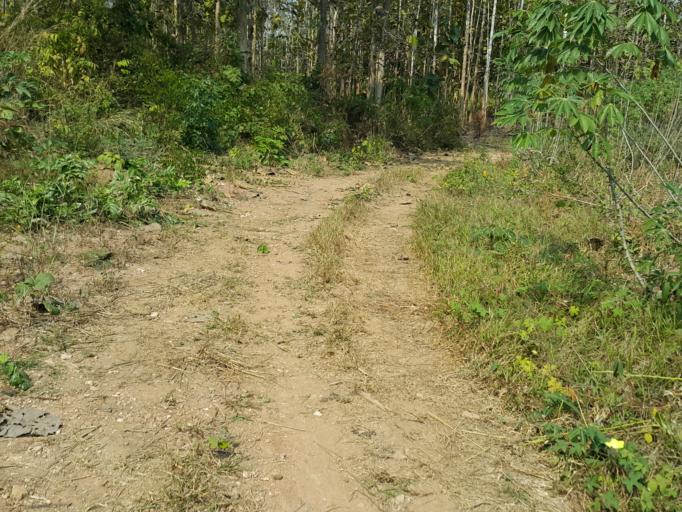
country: TH
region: Sukhothai
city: Thung Saliam
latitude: 17.3285
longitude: 99.4920
